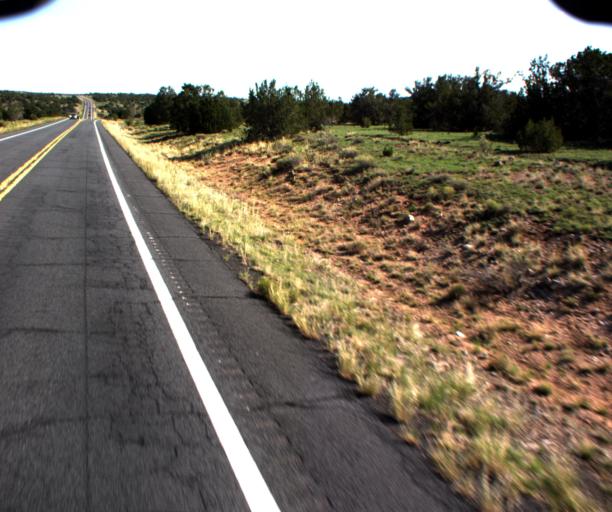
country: US
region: Arizona
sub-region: Coconino County
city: Williams
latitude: 35.4789
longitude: -112.1772
